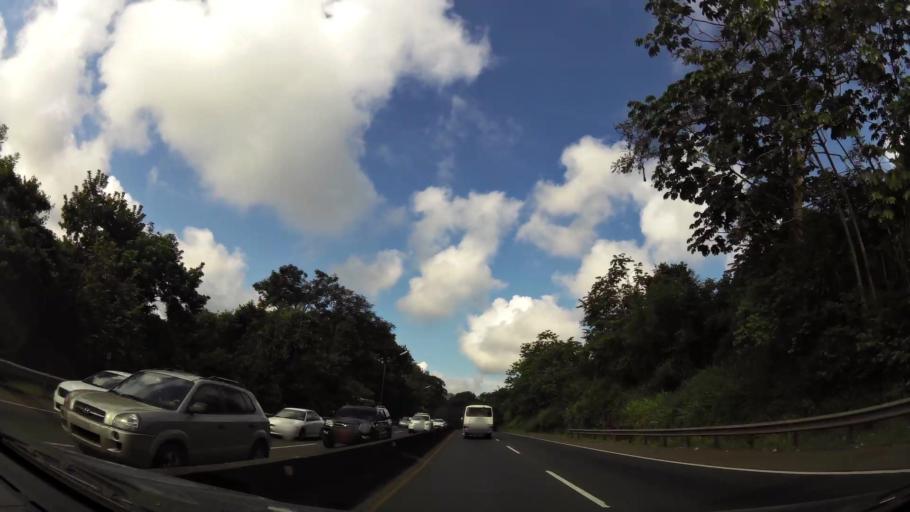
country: PA
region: Panama
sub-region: Distrito Arraijan
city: Arraijan
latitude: 8.9576
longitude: -79.6050
